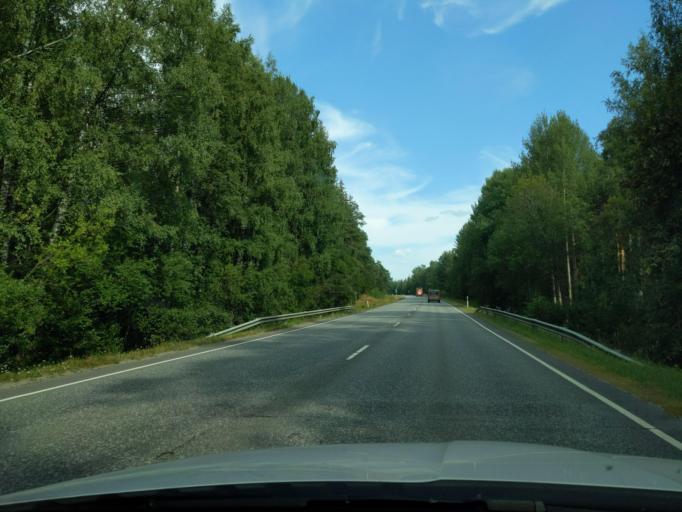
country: FI
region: Haeme
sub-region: Haemeenlinna
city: Hauho
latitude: 61.1751
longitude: 24.5744
